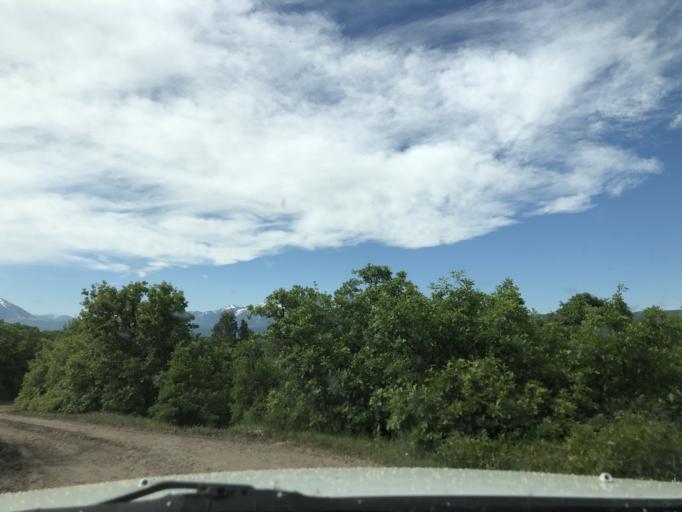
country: US
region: Colorado
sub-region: Delta County
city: Paonia
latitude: 39.0259
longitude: -107.3443
